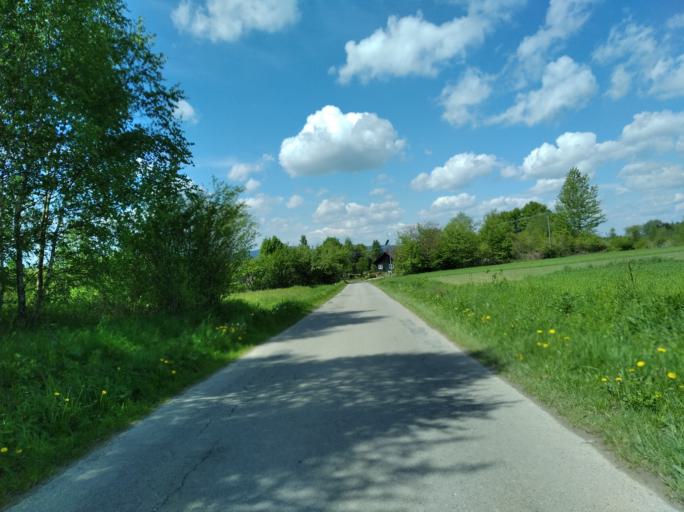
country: PL
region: Subcarpathian Voivodeship
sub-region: Powiat jasielski
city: Kolaczyce
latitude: 49.8420
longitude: 21.4676
